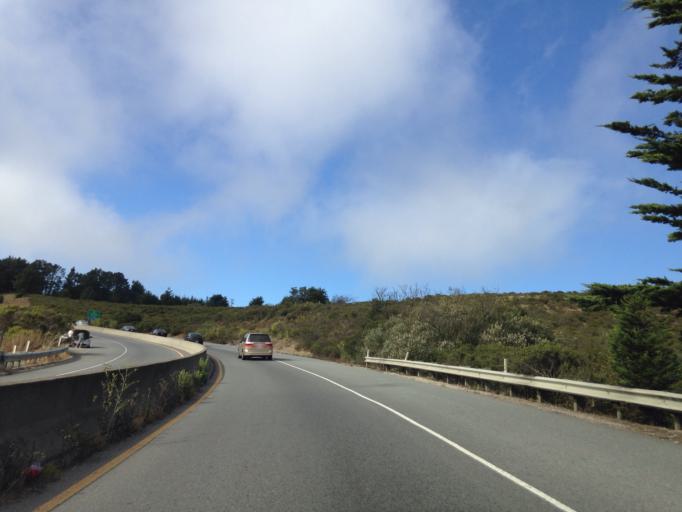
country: US
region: California
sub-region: San Mateo County
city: Highlands-Baywood Park
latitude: 37.4909
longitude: -122.3698
